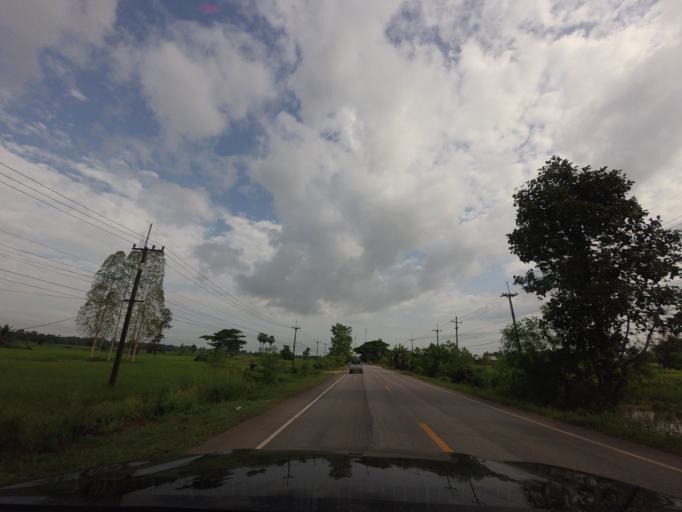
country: TH
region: Changwat Udon Thani
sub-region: Amphoe Ban Phue
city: Ban Phue
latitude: 17.7622
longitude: 102.3975
